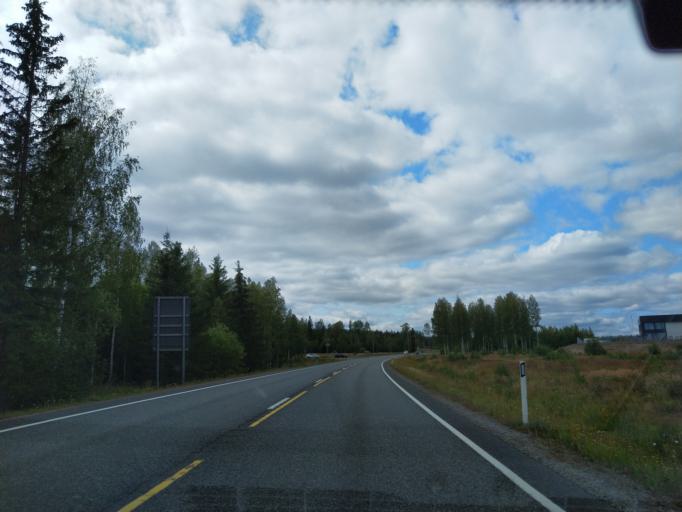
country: FI
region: Haeme
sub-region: Riihimaeki
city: Riihimaeki
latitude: 60.7426
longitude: 24.6927
